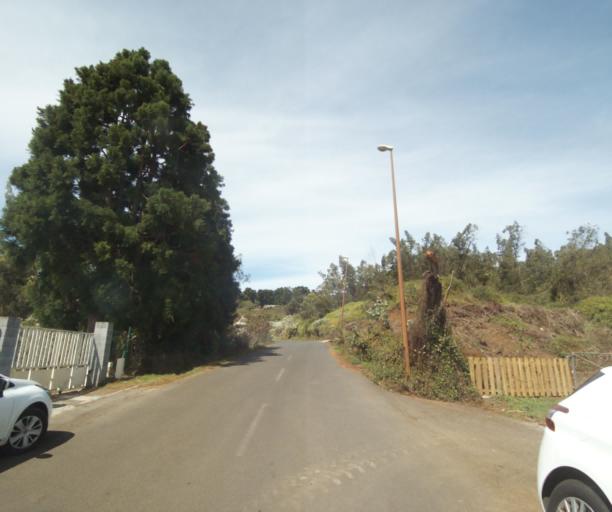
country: RE
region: Reunion
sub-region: Reunion
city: Trois-Bassins
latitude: -21.0488
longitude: 55.3406
